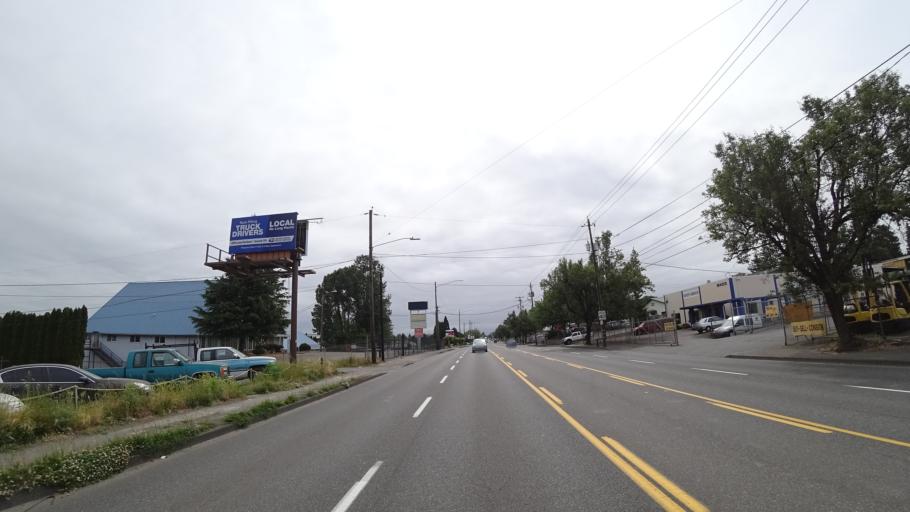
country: US
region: Oregon
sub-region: Multnomah County
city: Portland
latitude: 45.5699
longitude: -122.6081
